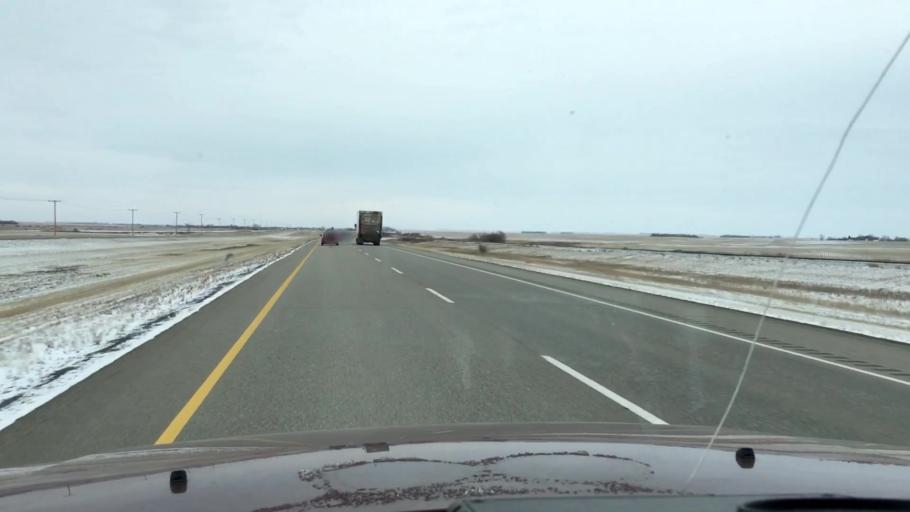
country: CA
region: Saskatchewan
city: Watrous
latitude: 51.1868
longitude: -105.9447
